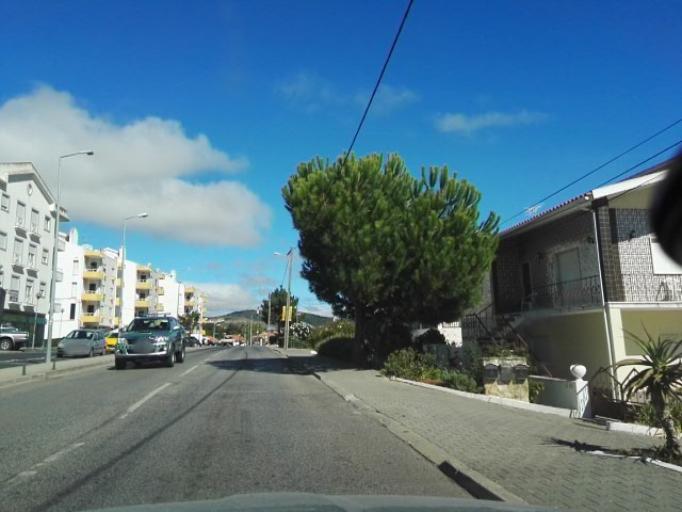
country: PT
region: Lisbon
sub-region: Arruda Dos Vinhos
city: Arruda dos Vinhos
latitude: 38.9895
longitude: -9.0797
